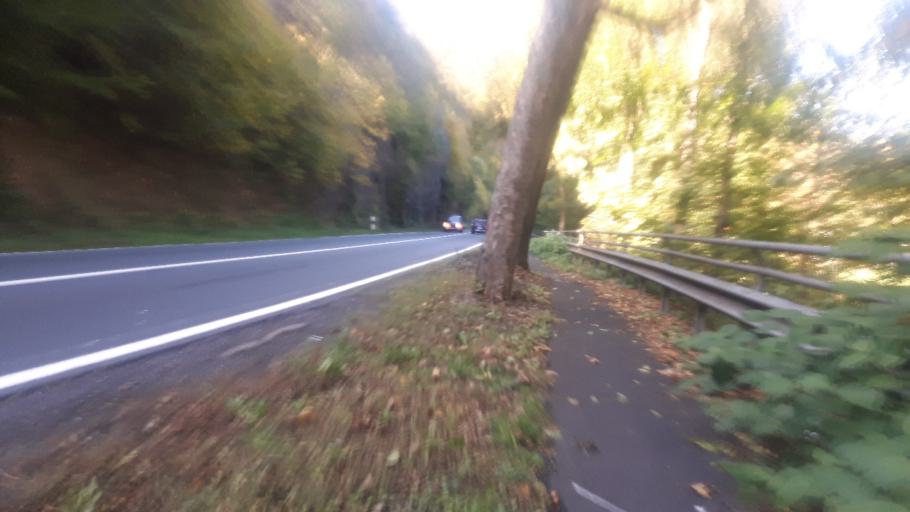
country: DE
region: Rheinland-Pfalz
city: Wissen
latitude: 50.7853
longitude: 7.7530
